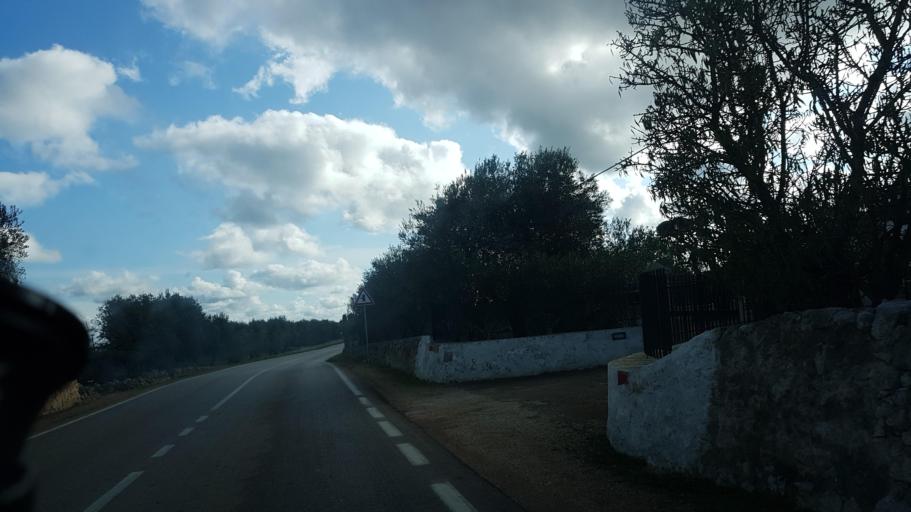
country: IT
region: Apulia
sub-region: Provincia di Brindisi
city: San Michele Salentino
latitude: 40.6720
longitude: 17.5967
